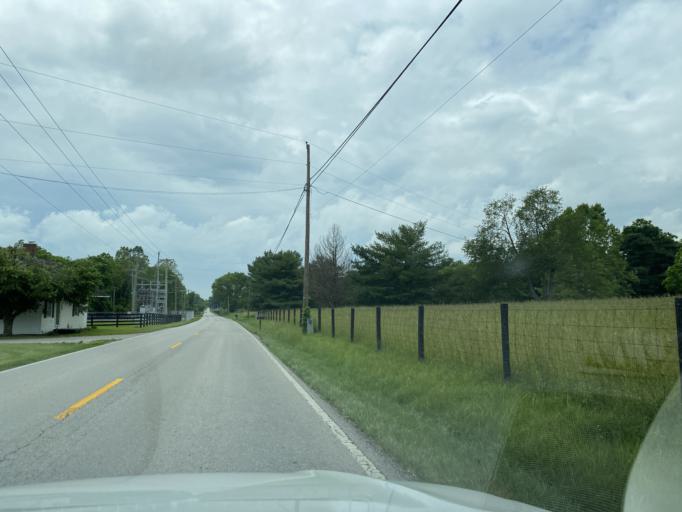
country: US
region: Kentucky
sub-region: Scott County
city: Georgetown
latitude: 38.2219
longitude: -84.4569
